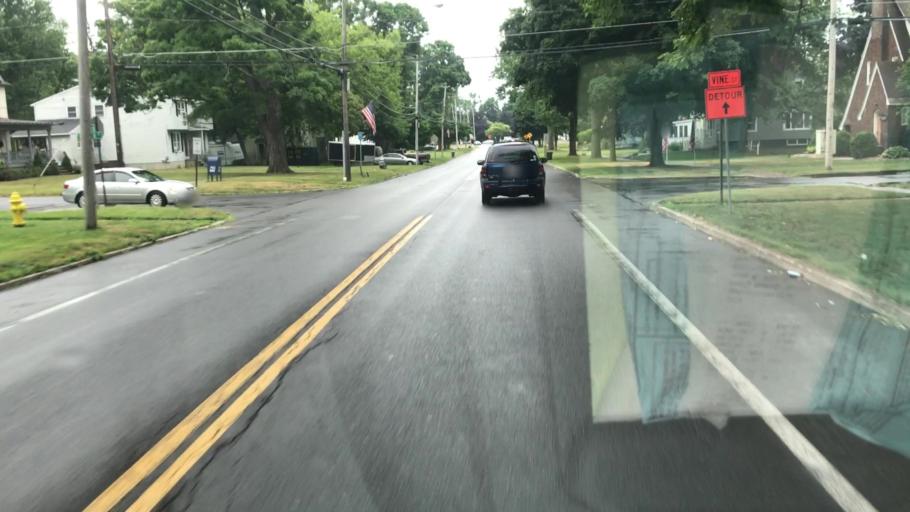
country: US
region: New York
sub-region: Onondaga County
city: Liverpool
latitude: 43.1069
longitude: -76.2093
